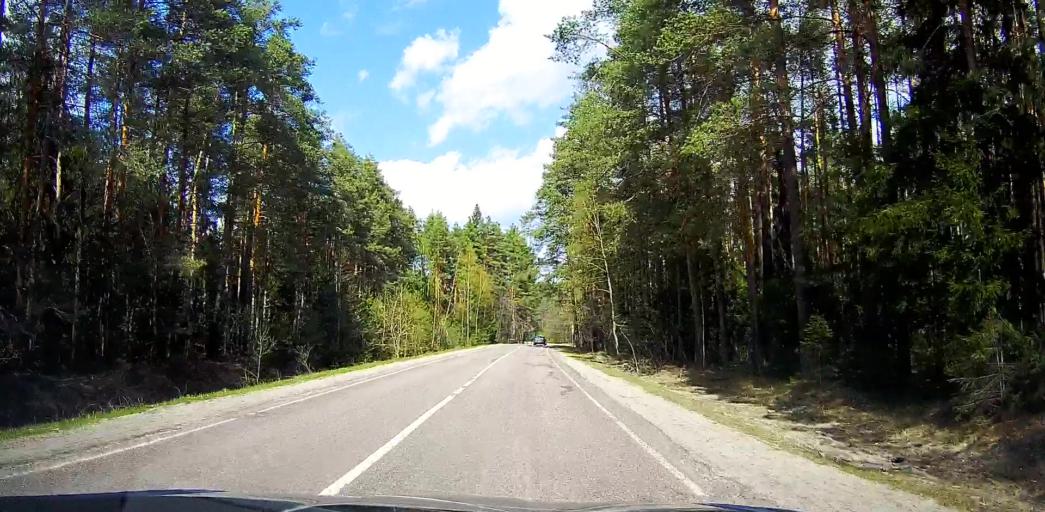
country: RU
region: Moskovskaya
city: Davydovo
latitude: 55.5680
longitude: 38.8220
